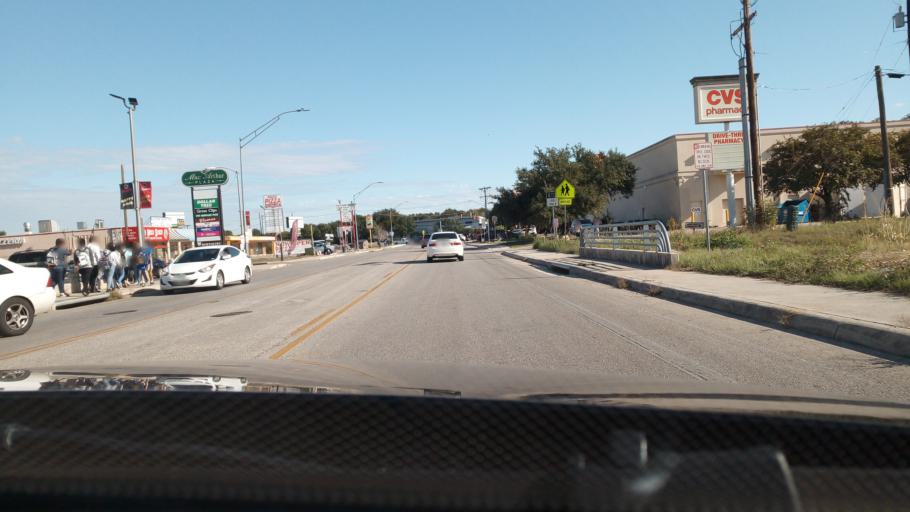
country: US
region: Texas
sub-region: Bexar County
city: Alamo Heights
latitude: 29.5273
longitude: -98.4408
